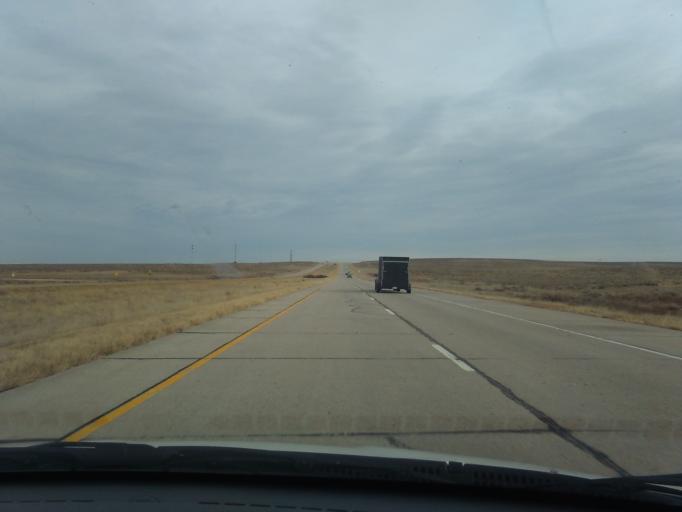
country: US
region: Colorado
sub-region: Weld County
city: Keenesburg
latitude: 40.2181
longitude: -104.2084
